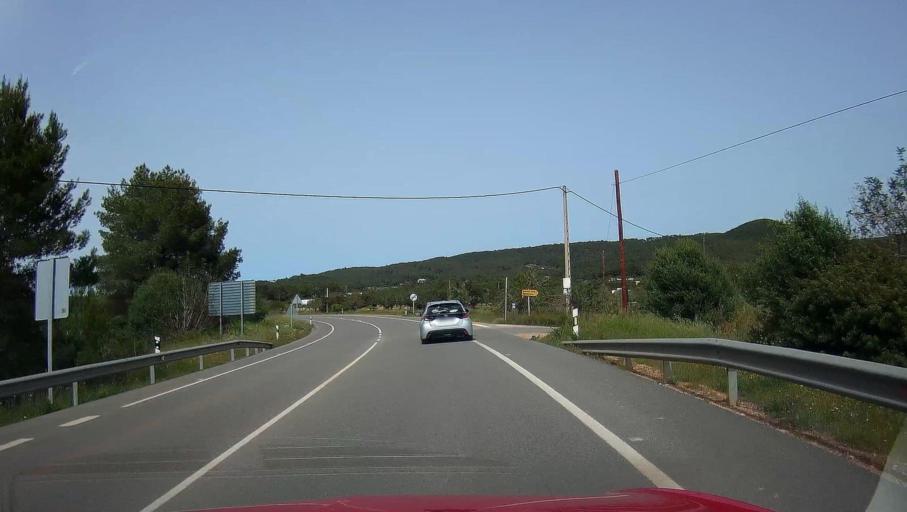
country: ES
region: Balearic Islands
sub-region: Illes Balears
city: Sant Joan de Labritja
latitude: 39.0527
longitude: 1.4920
